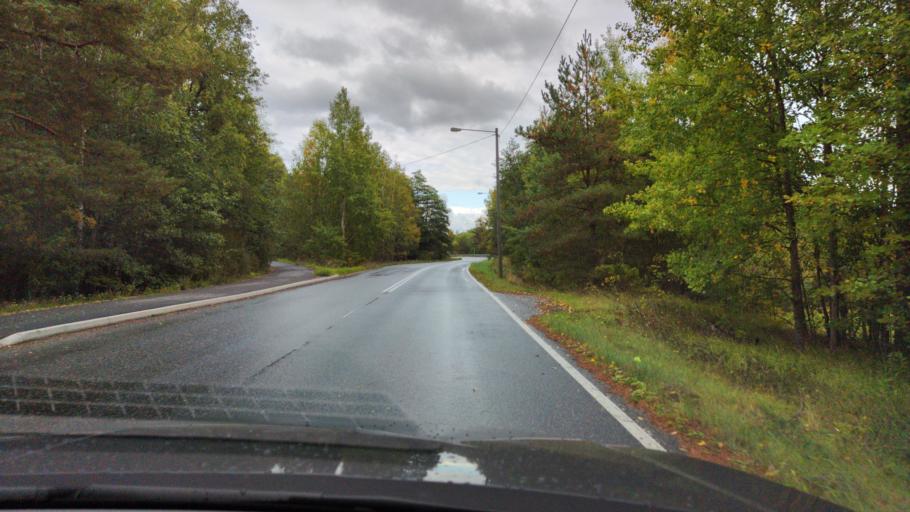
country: FI
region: Varsinais-Suomi
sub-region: Aboland-Turunmaa
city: Pargas
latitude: 60.3658
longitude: 22.2305
